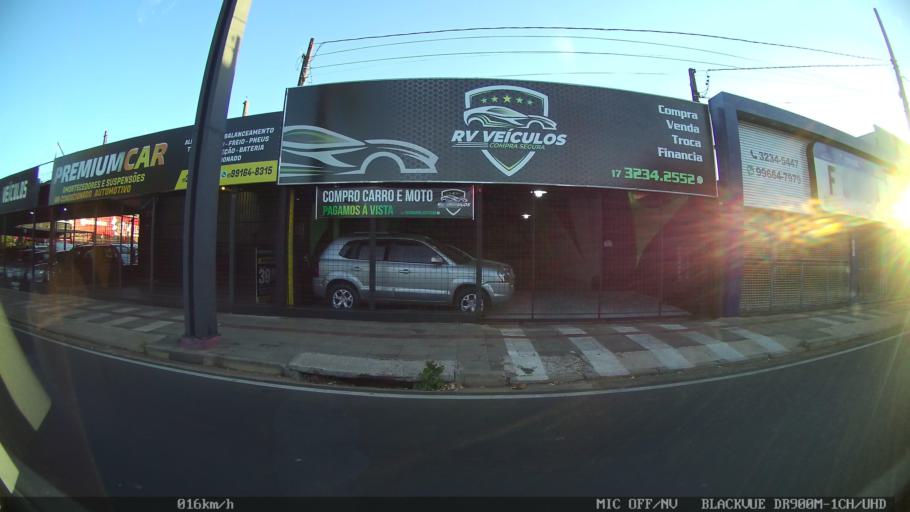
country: BR
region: Sao Paulo
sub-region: Sao Jose Do Rio Preto
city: Sao Jose do Rio Preto
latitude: -20.7860
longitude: -49.3775
